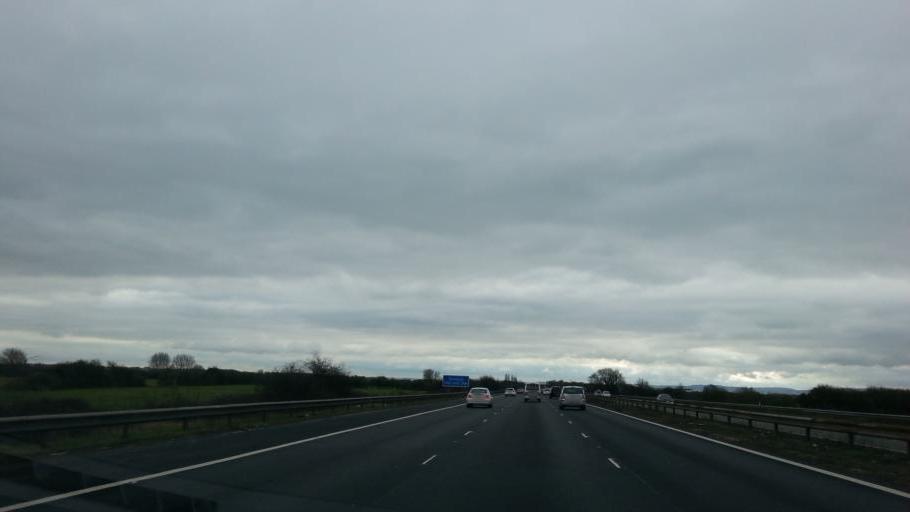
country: GB
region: England
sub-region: Somerset
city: Highbridge
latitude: 51.2271
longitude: -2.9530
